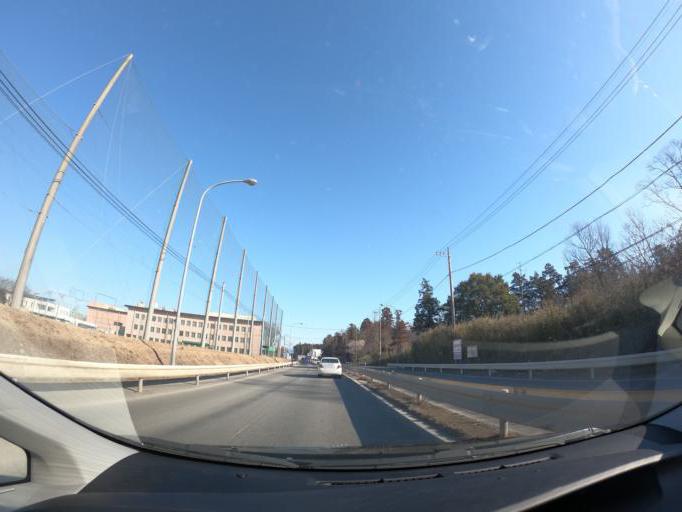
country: JP
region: Ibaraki
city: Ishige
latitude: 36.1024
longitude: 140.0379
